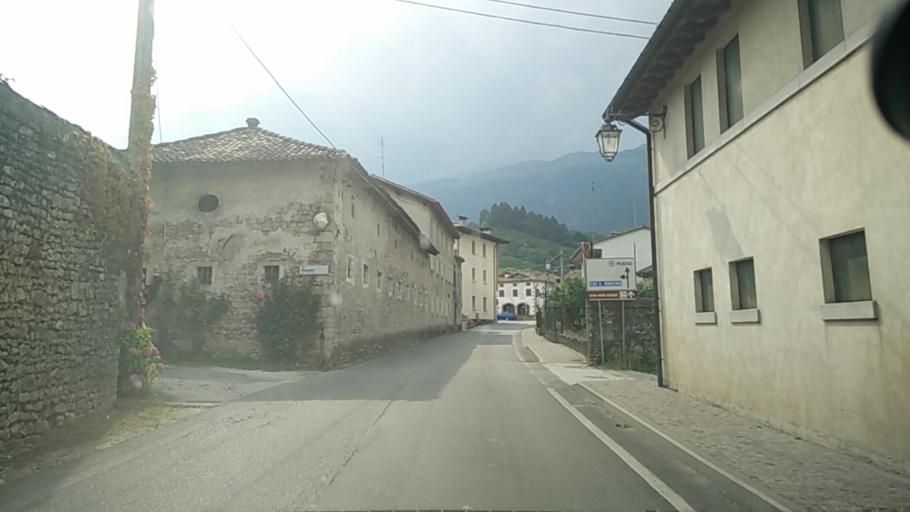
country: IT
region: Veneto
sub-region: Provincia di Treviso
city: Miane
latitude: 45.9300
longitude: 12.1085
